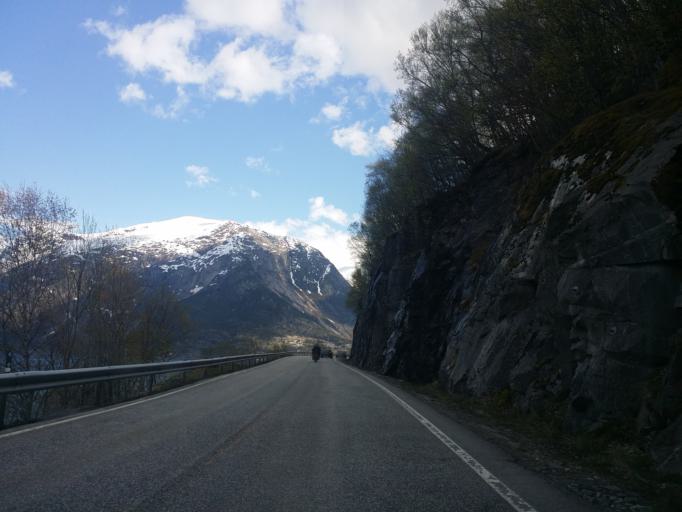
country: NO
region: Hordaland
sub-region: Eidfjord
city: Eidfjord
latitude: 60.4788
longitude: 7.0235
